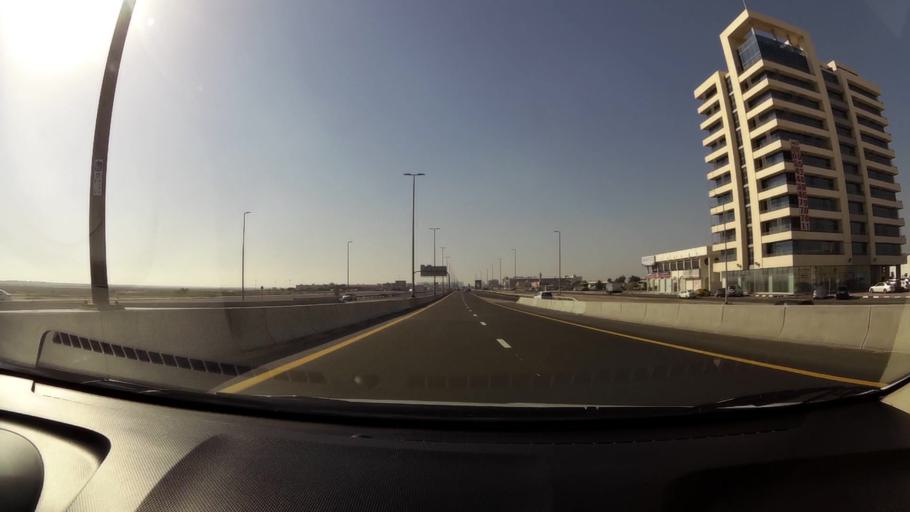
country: AE
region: Umm al Qaywayn
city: Umm al Qaywayn
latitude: 25.4978
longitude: 55.5518
